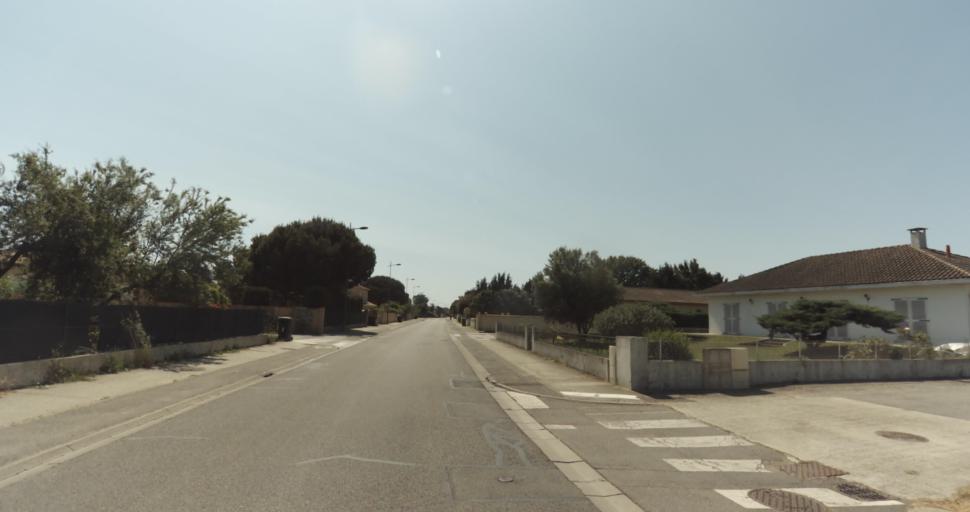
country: FR
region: Midi-Pyrenees
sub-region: Departement de la Haute-Garonne
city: La Salvetat-Saint-Gilles
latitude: 43.5827
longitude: 1.2798
